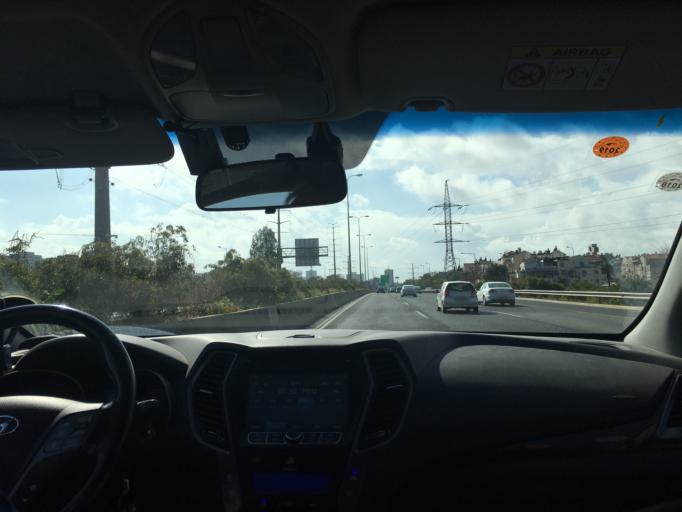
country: IL
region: Tel Aviv
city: Giv`at Shemu'el
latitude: 32.0925
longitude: 34.8458
